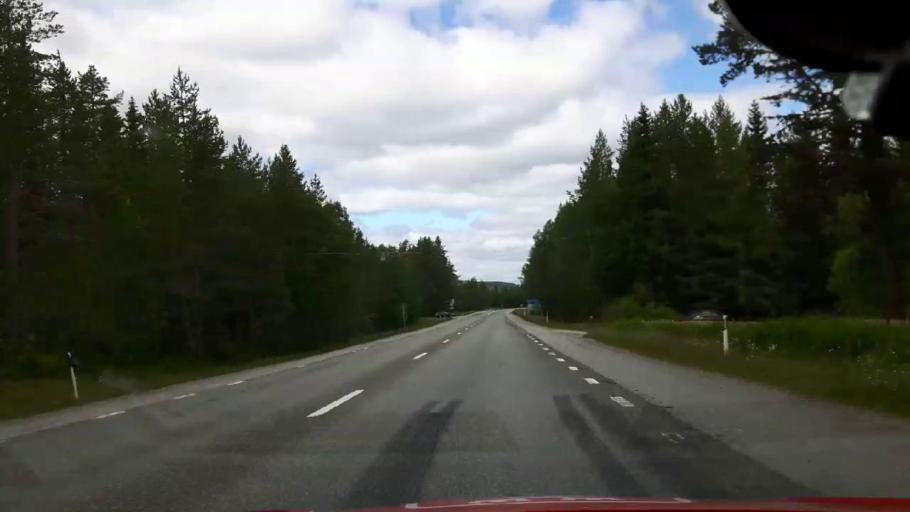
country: SE
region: Jaemtland
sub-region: Braecke Kommun
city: Braecke
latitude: 62.7144
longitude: 15.4637
